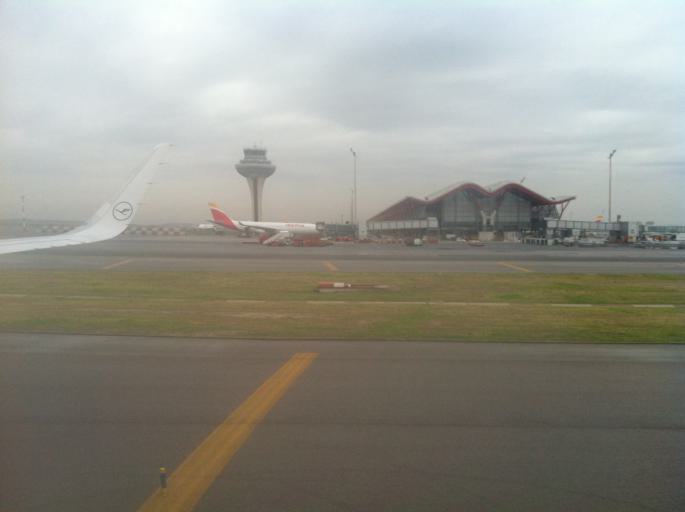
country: ES
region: Madrid
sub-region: Provincia de Madrid
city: Barajas de Madrid
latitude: 40.4878
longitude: -3.5682
